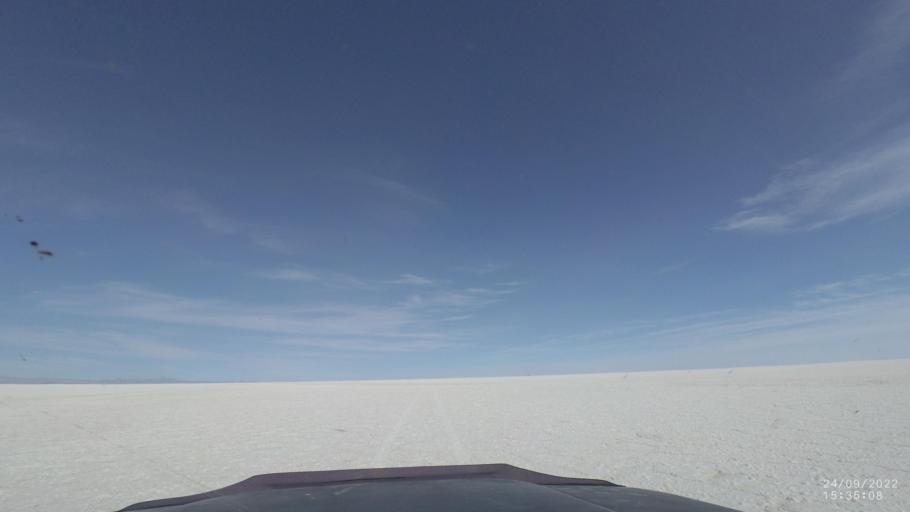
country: BO
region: Potosi
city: Colchani
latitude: -20.1318
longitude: -67.2566
